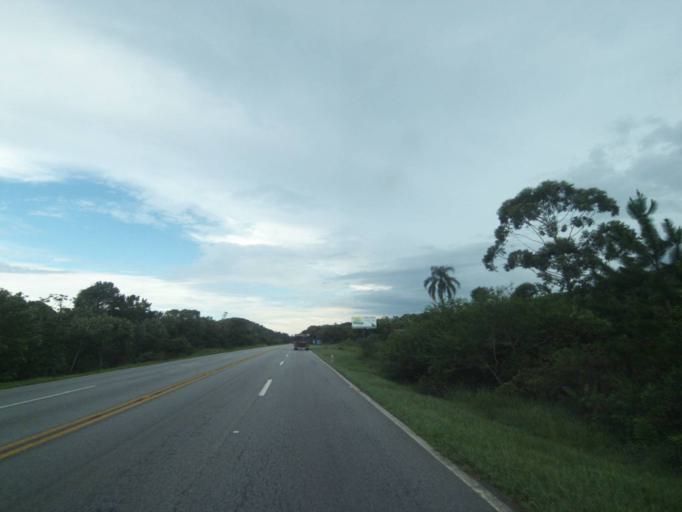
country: BR
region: Parana
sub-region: Pontal Do Parana
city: Pontal do Parana
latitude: -25.6706
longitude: -48.5808
